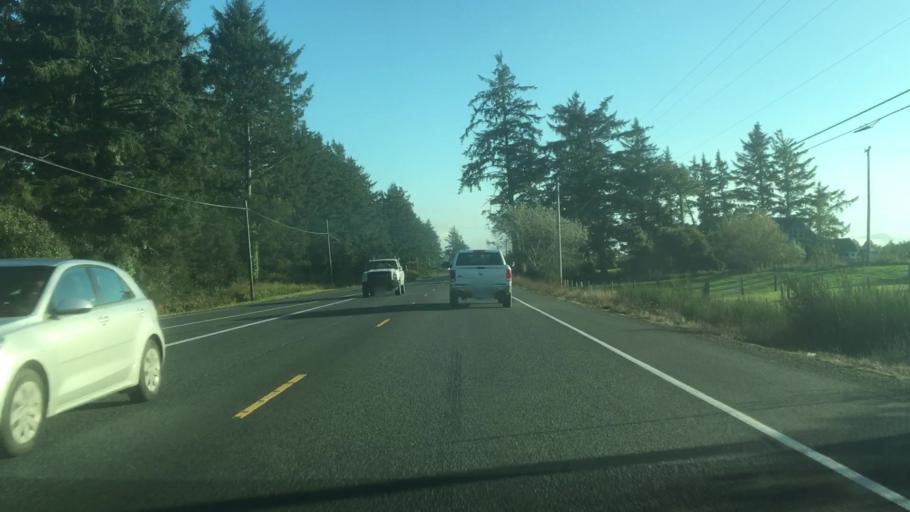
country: US
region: Oregon
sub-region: Clatsop County
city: Gearhart
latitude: 46.0881
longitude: -123.9163
